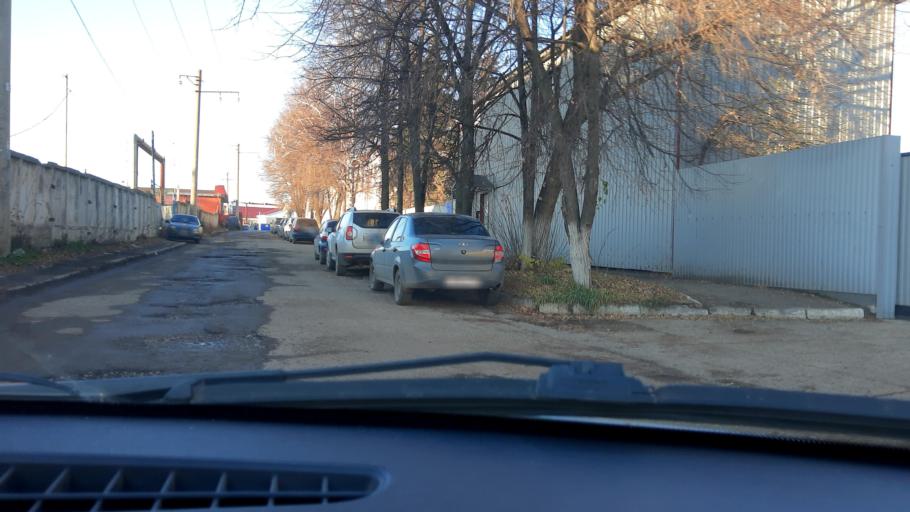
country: RU
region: Bashkortostan
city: Mikhaylovka
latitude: 54.6929
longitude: 55.8436
